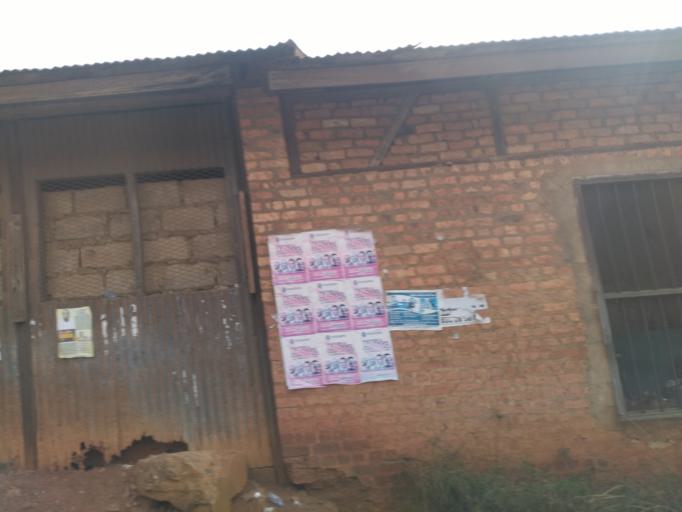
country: GH
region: Ashanti
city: Kumasi
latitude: 6.6886
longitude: -1.6242
